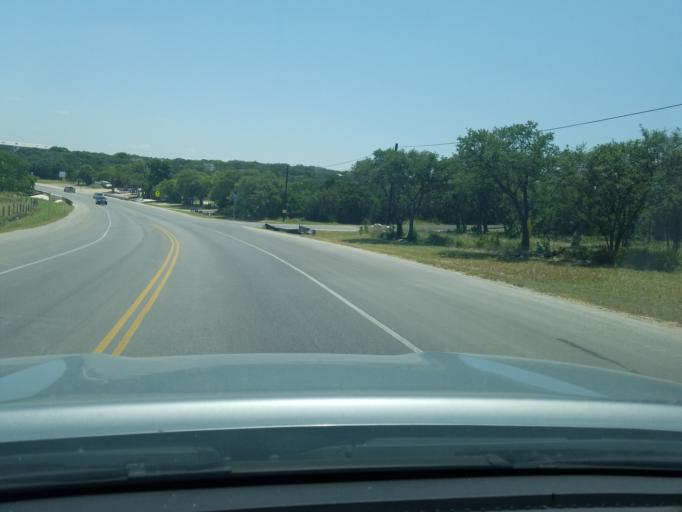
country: US
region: Texas
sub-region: Bexar County
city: Timberwood Park
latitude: 29.7072
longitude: -98.5165
